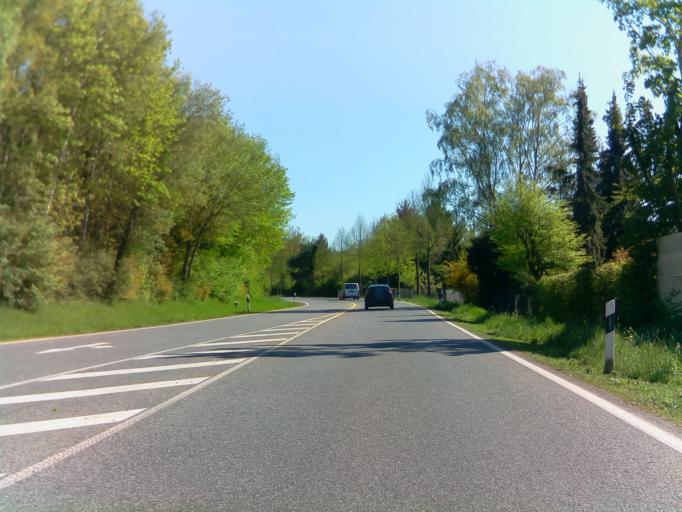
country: DE
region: Hesse
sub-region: Regierungsbezirk Giessen
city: Alsfeld
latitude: 50.7340
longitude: 9.2817
